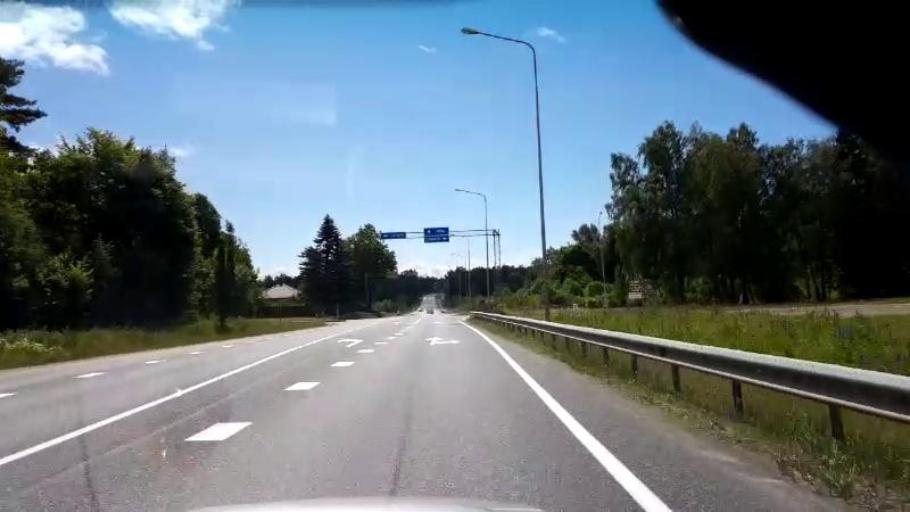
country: LV
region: Saulkrastu
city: Saulkrasti
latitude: 57.4700
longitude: 24.4348
